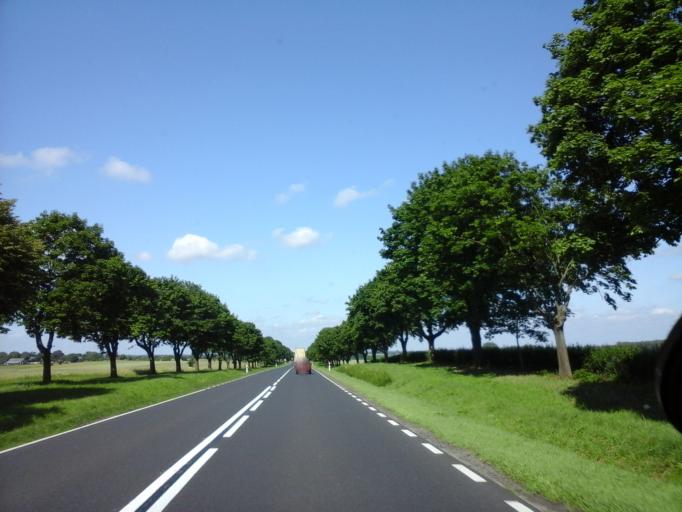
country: PL
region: West Pomeranian Voivodeship
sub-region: Powiat stargardzki
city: Dobrzany
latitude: 53.2730
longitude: 15.4234
